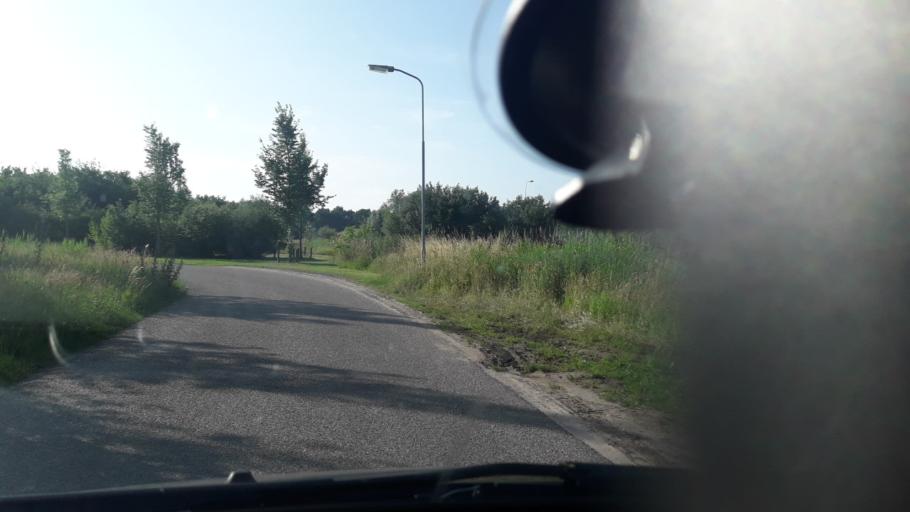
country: NL
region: Gelderland
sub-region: Gemeente Ermelo
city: Horst
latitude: 52.3230
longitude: 5.5807
